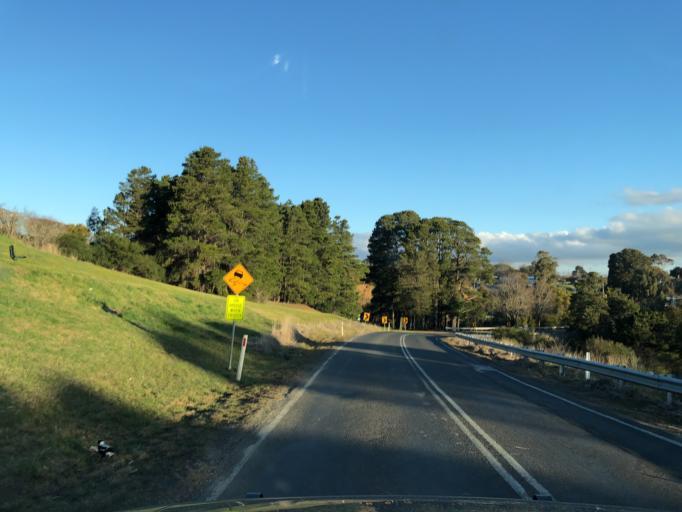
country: AU
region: Victoria
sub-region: Moorabool
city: Bacchus Marsh
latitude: -37.5968
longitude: 144.2311
